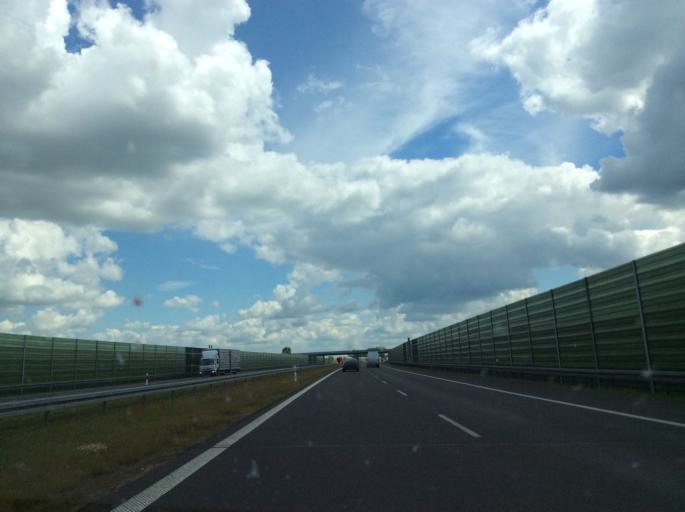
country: PL
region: Greater Poland Voivodeship
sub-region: Powiat kolski
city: Grzegorzew
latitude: 52.1142
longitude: 18.7334
